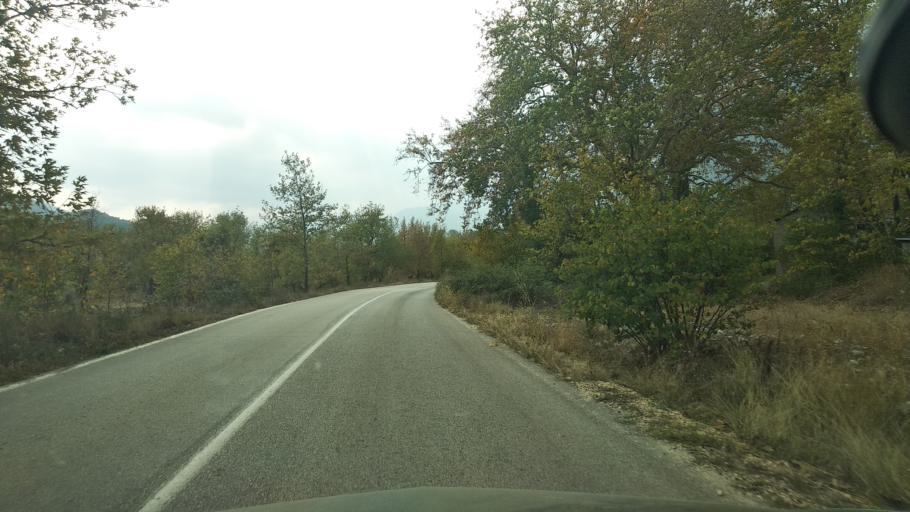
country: GR
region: Thessaly
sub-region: Trikala
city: Kastraki
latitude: 39.6987
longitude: 21.5243
